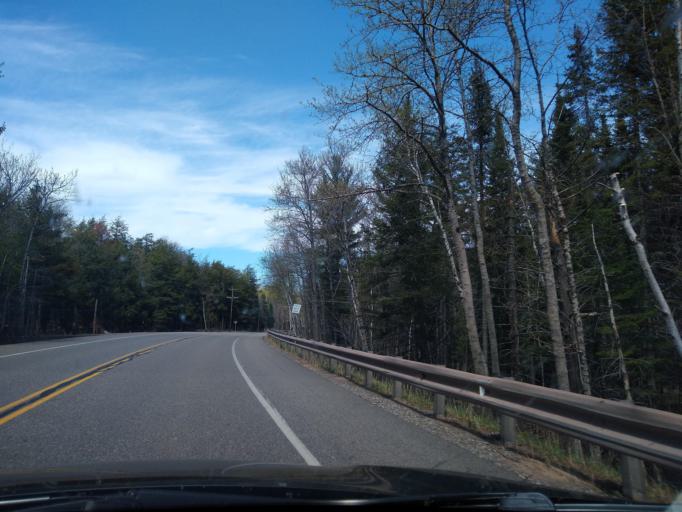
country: US
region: Michigan
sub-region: Marquette County
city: Trowbridge Park
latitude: 46.6235
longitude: -87.4695
